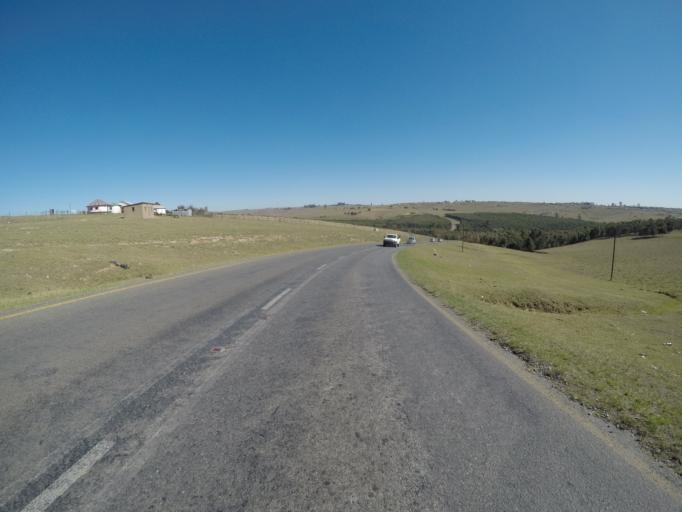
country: ZA
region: Eastern Cape
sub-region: OR Tambo District Municipality
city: Mthatha
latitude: -31.7817
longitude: 28.7384
